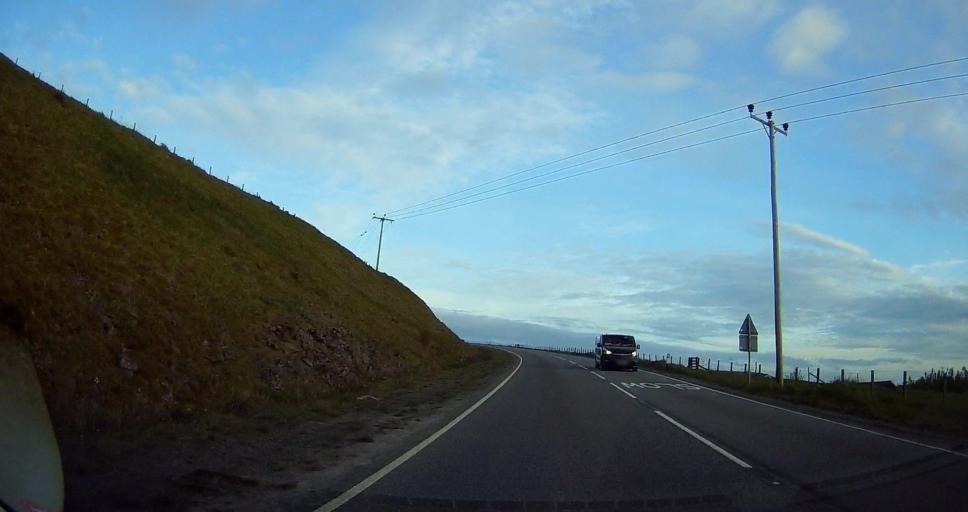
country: GB
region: Scotland
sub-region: Shetland Islands
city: Lerwick
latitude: 60.1824
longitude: -1.2246
